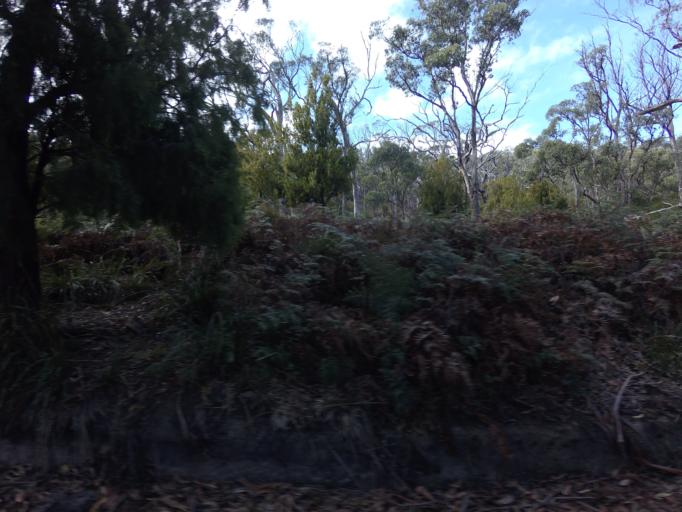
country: AU
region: Tasmania
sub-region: Clarence
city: Sandford
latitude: -43.0781
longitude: 147.6683
